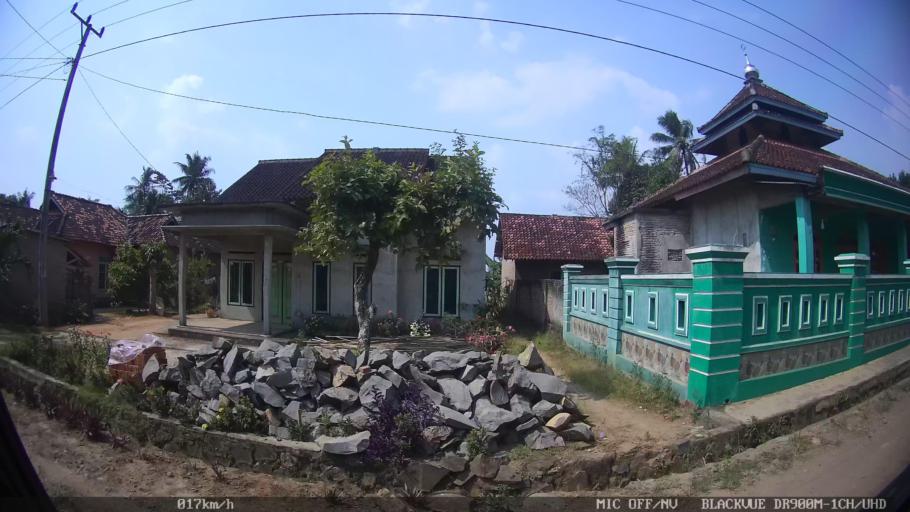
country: ID
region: Lampung
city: Natar
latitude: -5.2947
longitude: 105.2447
